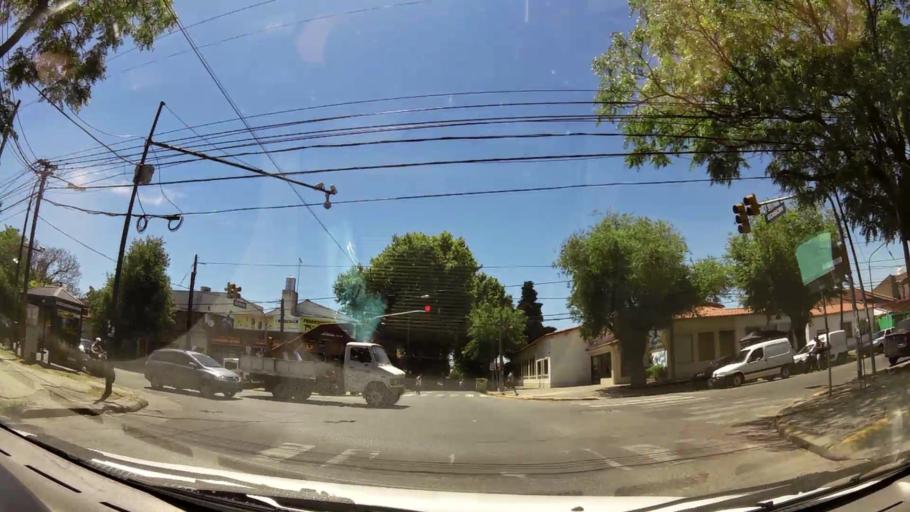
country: AR
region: Buenos Aires
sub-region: Partido de Vicente Lopez
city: Olivos
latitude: -34.5015
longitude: -58.5180
